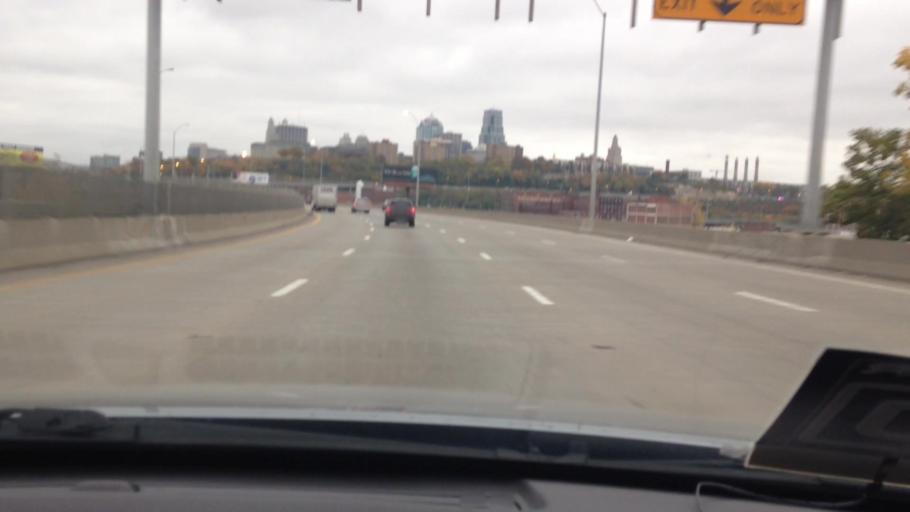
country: US
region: Kansas
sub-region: Wyandotte County
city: Kansas City
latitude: 39.1076
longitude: -94.6039
